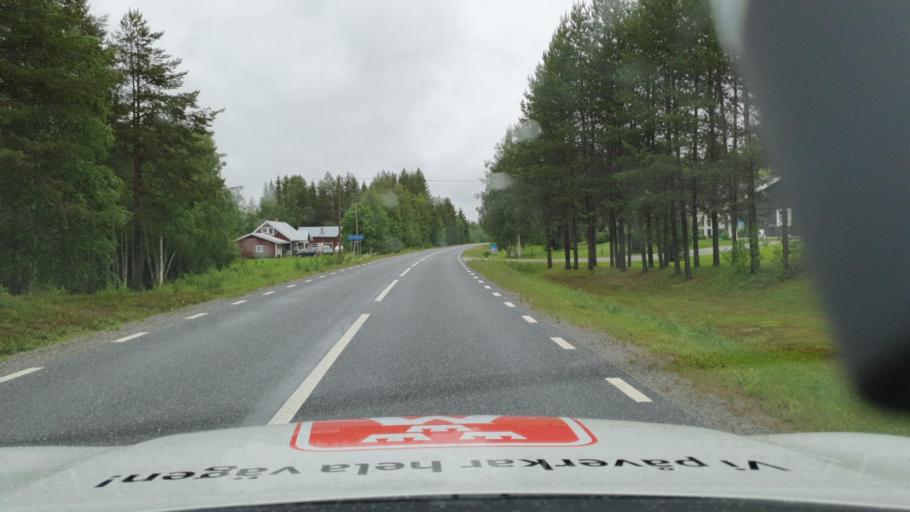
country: SE
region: Vaesterbotten
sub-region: Asele Kommun
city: Asele
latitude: 63.9955
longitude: 17.2642
